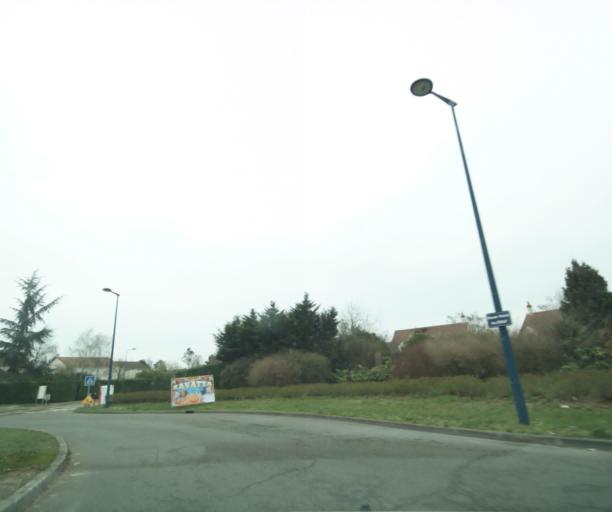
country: FR
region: Ile-de-France
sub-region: Departement du Val-d'Oise
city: Courdimanche
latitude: 49.0399
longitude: 2.0161
